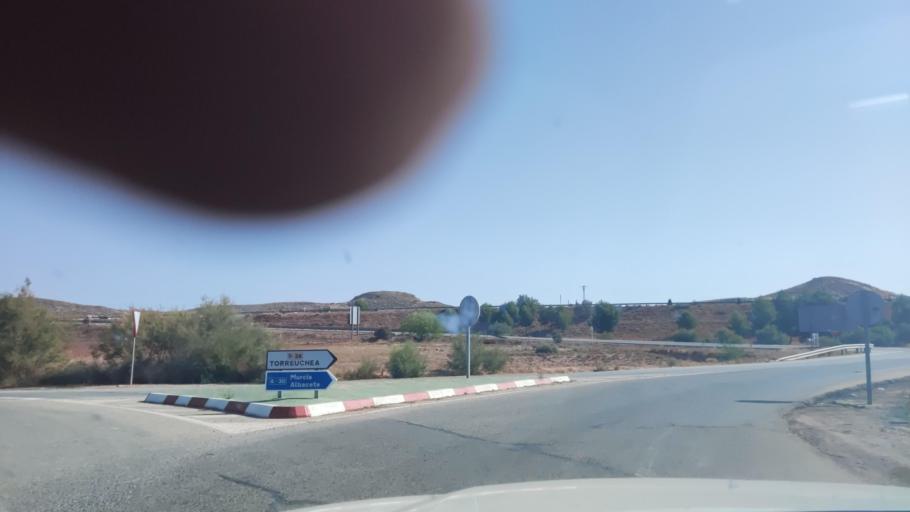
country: ES
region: Castille-La Mancha
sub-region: Provincia de Albacete
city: Hellin
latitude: 38.4938
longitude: -1.6421
